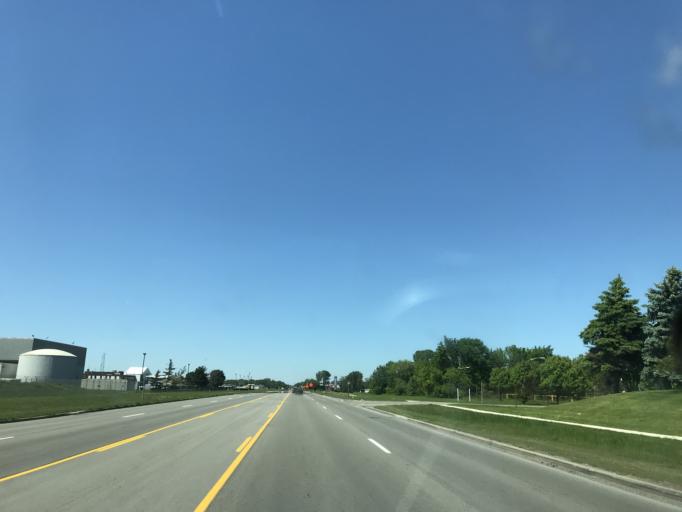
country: US
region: Michigan
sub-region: Wayne County
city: Taylor
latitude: 42.2267
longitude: -83.3273
